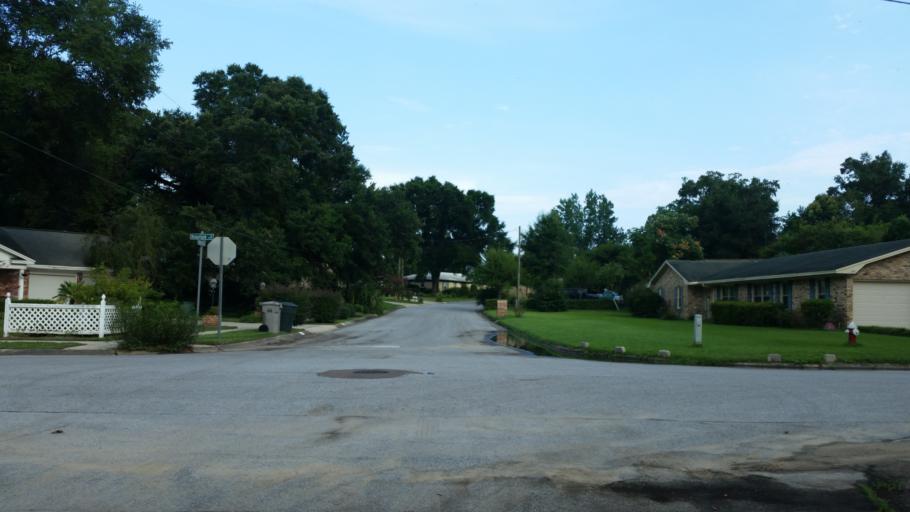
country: US
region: Florida
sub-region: Escambia County
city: Ferry Pass
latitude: 30.5142
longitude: -87.1893
